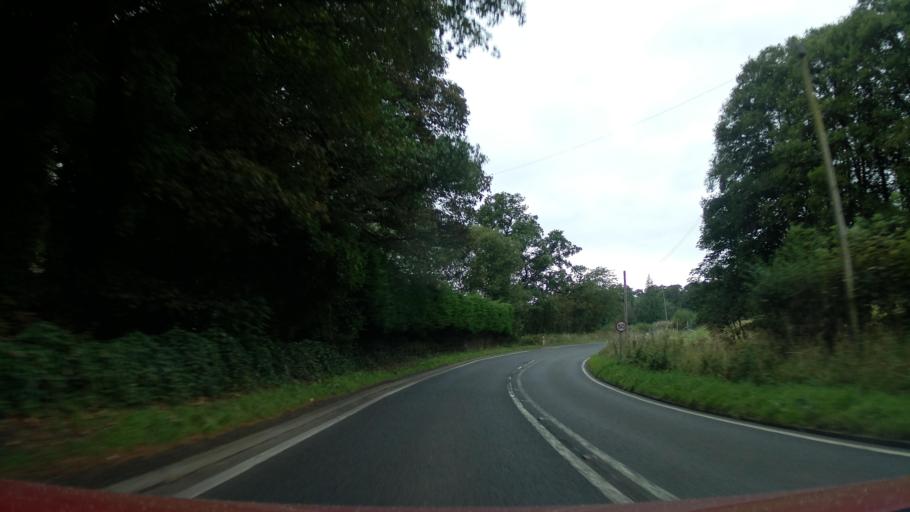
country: GB
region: Scotland
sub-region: Clackmannanshire
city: Dollar
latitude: 56.1594
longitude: -3.7029
